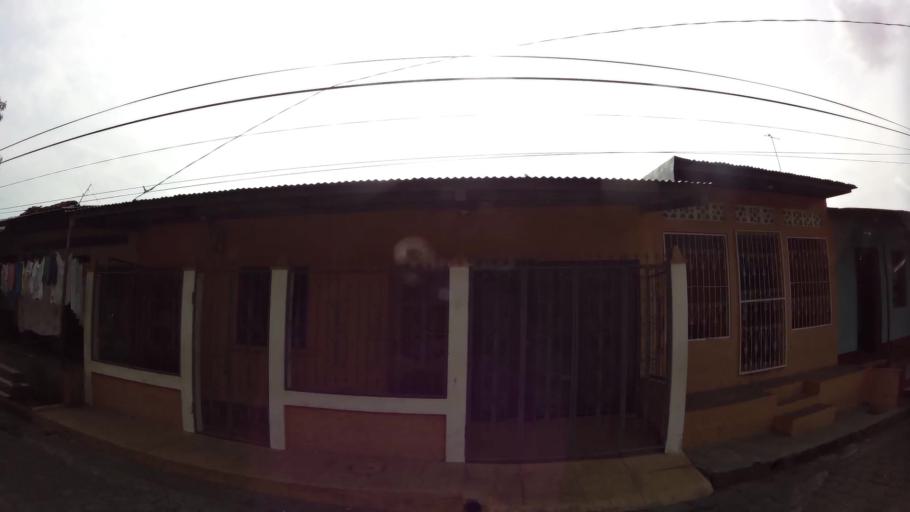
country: NI
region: Masaya
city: Masaya
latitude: 11.9693
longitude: -86.0925
